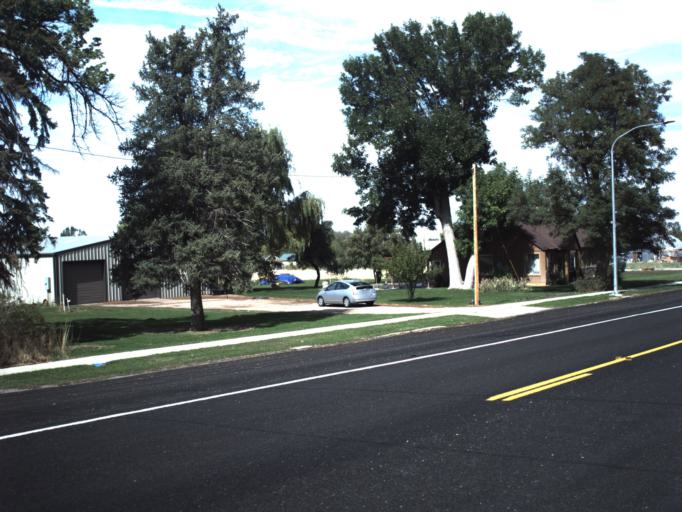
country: US
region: Utah
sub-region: Millard County
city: Fillmore
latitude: 38.7949
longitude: -112.4376
